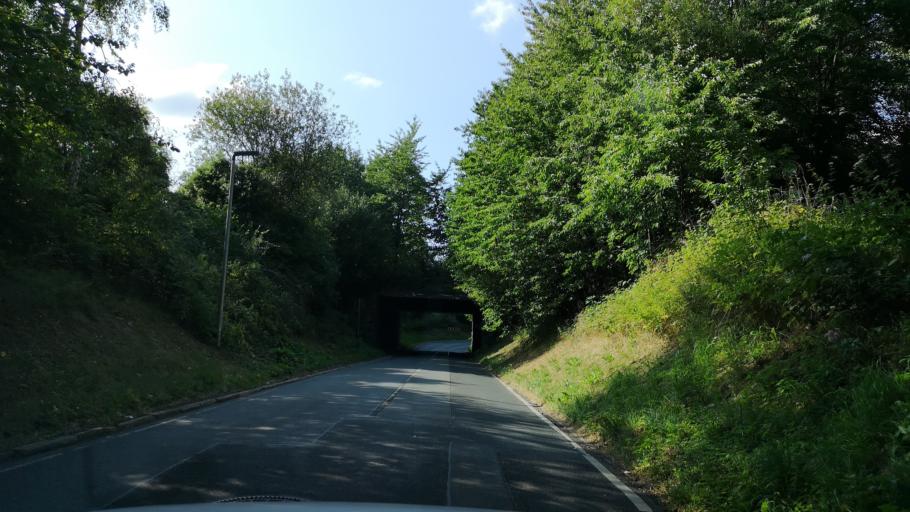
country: DE
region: North Rhine-Westphalia
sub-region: Regierungsbezirk Arnsberg
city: Holzwickede
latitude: 51.4587
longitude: 7.6243
